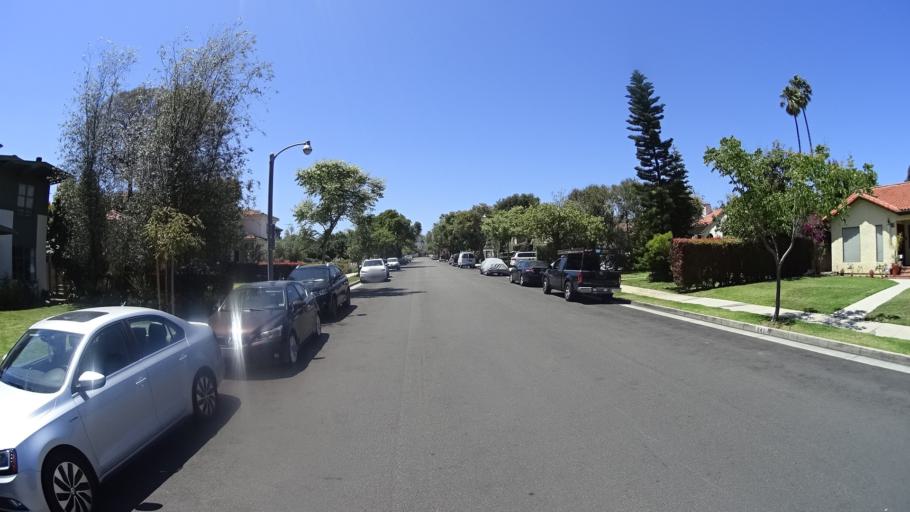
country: US
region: California
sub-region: Los Angeles County
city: Santa Monica
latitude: 34.0361
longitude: -118.4850
